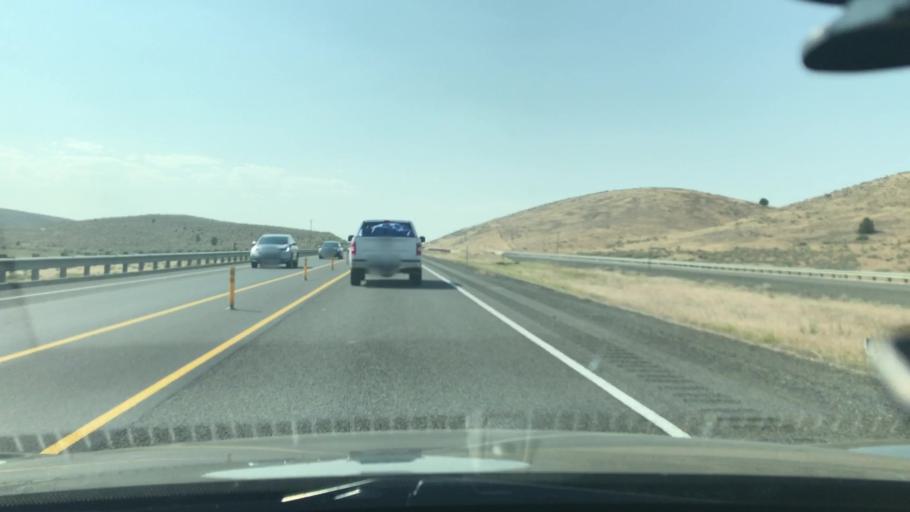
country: US
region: Oregon
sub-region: Baker County
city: Baker City
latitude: 44.6815
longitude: -117.6561
